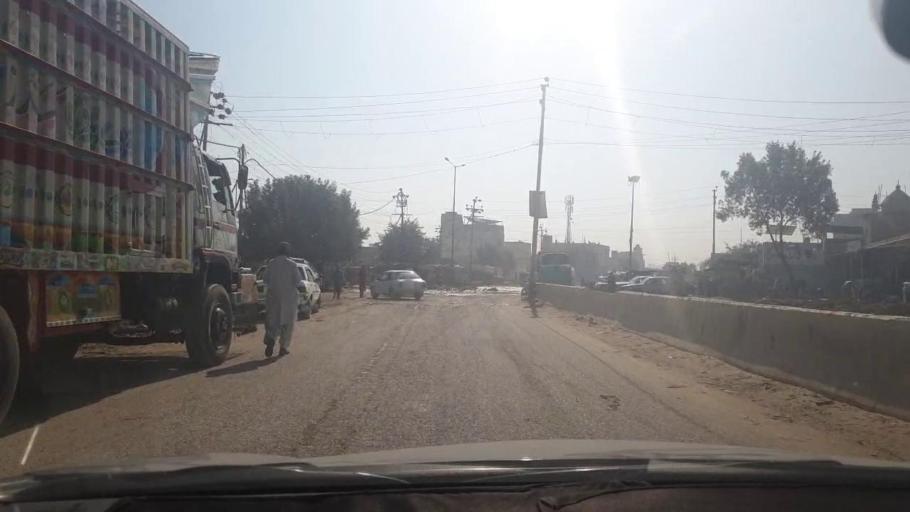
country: PK
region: Sindh
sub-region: Karachi District
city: Karachi
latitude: 25.0019
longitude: 67.0354
